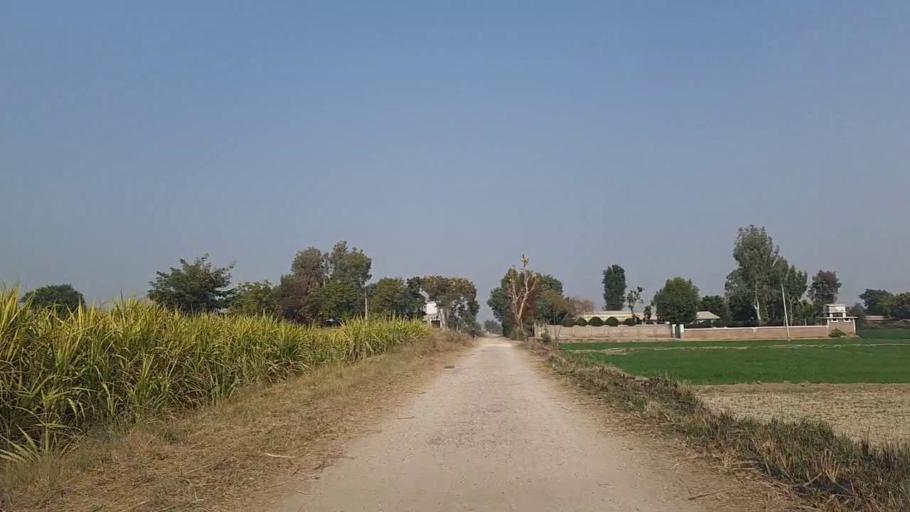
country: PK
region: Sindh
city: Daur
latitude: 26.4755
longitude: 68.4823
